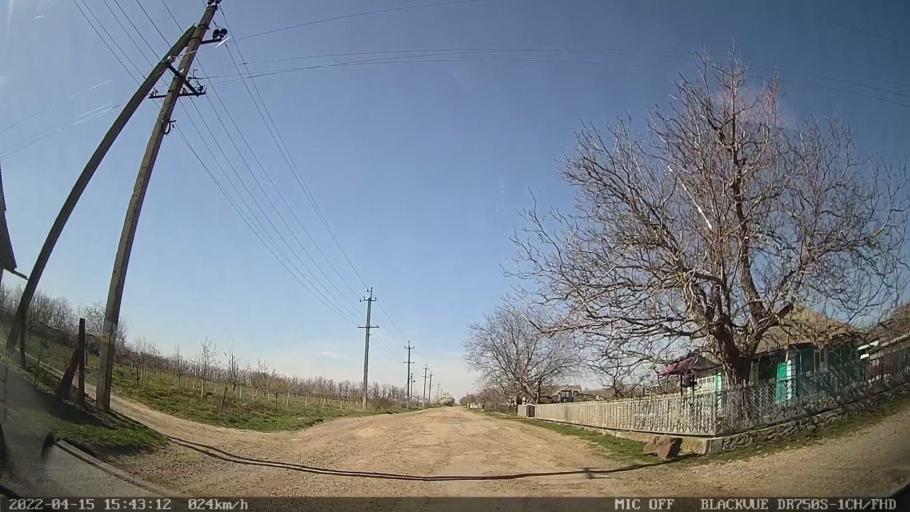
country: MD
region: Raionul Ocnita
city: Otaci
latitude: 48.3644
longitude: 27.9269
